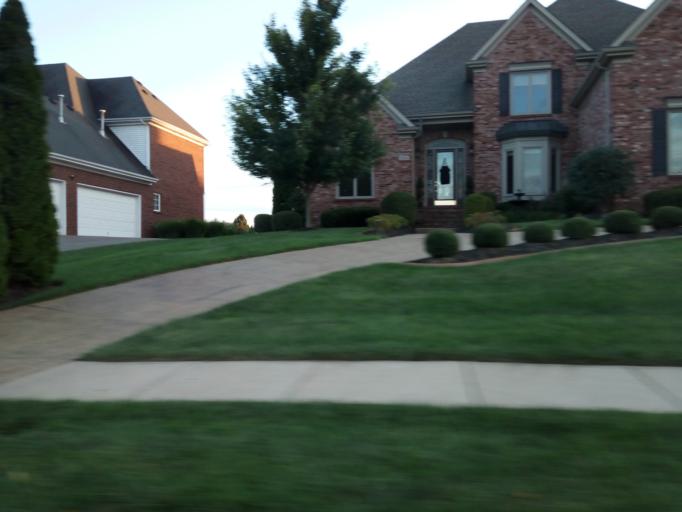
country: US
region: Kentucky
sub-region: Oldham County
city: Pewee Valley
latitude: 38.2742
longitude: -85.4842
